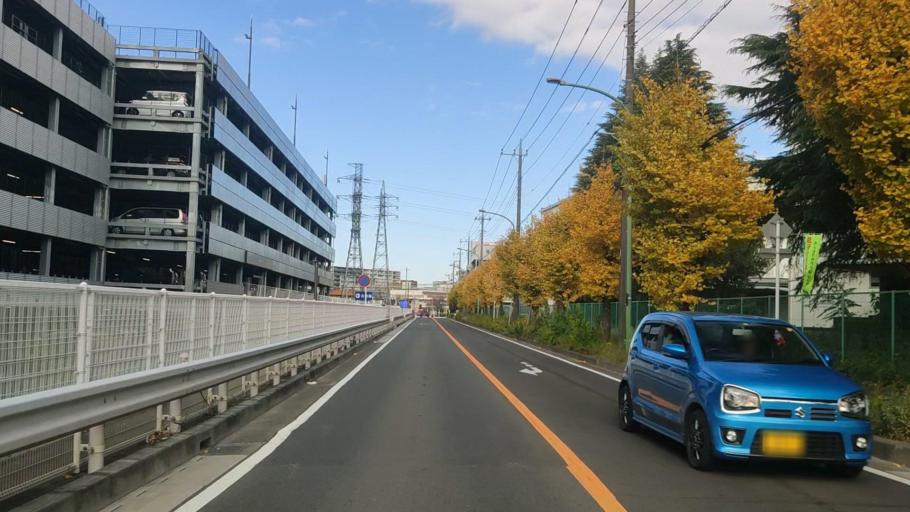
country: JP
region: Kanagawa
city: Minami-rinkan
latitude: 35.4994
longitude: 139.4257
